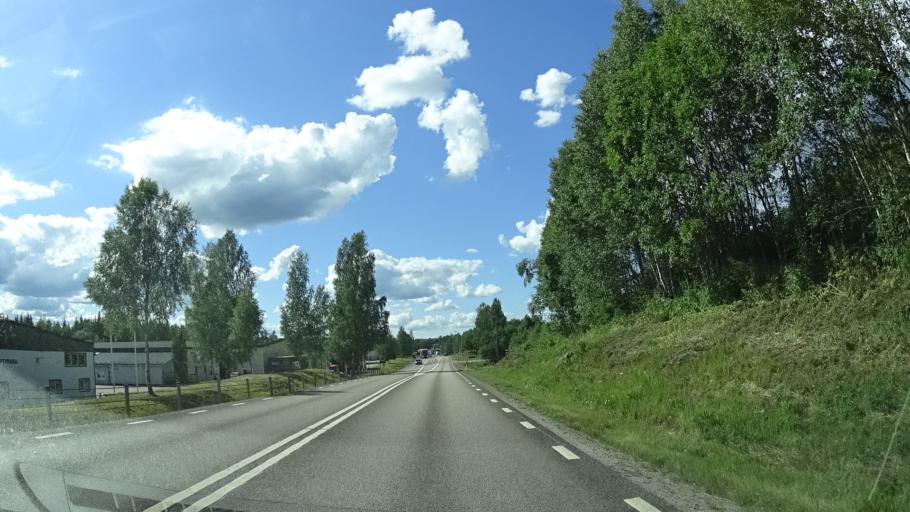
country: SE
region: Vaermland
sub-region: Arjangs Kommun
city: Toecksfors
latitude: 59.5045
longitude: 11.8651
